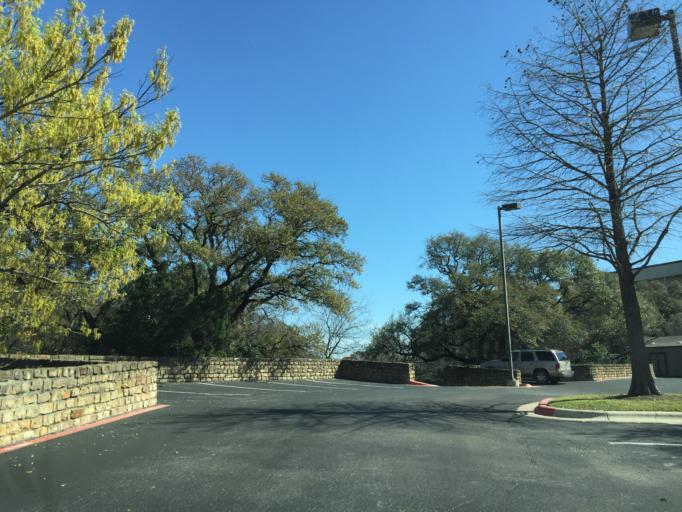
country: US
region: Texas
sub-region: Williamson County
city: Jollyville
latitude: 30.3936
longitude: -97.7387
